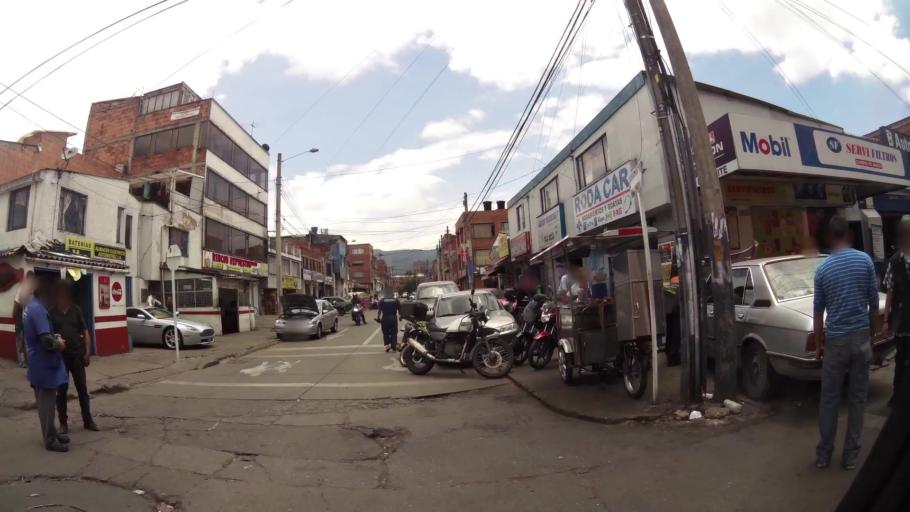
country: CO
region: Bogota D.C.
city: Barrio San Luis
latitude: 4.7174
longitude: -74.0540
